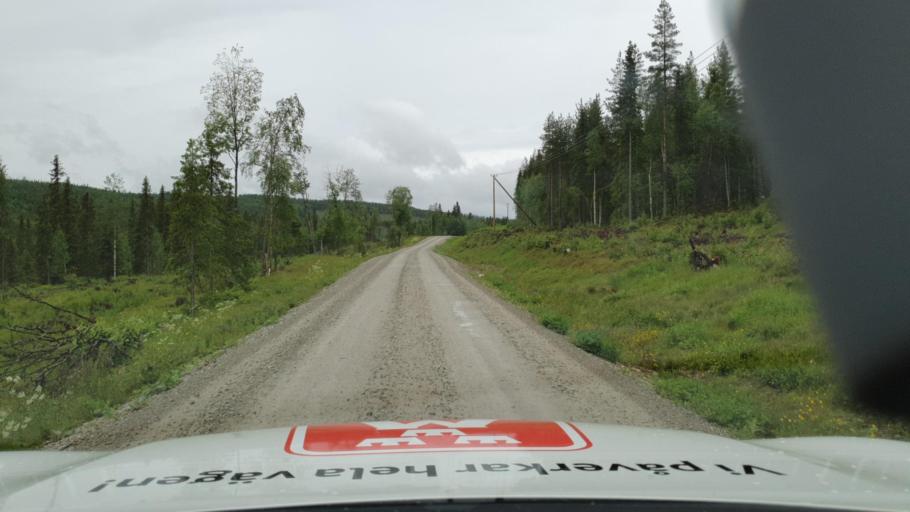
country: SE
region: Vaesterbotten
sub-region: Asele Kommun
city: Asele
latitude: 63.9697
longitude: 16.9094
